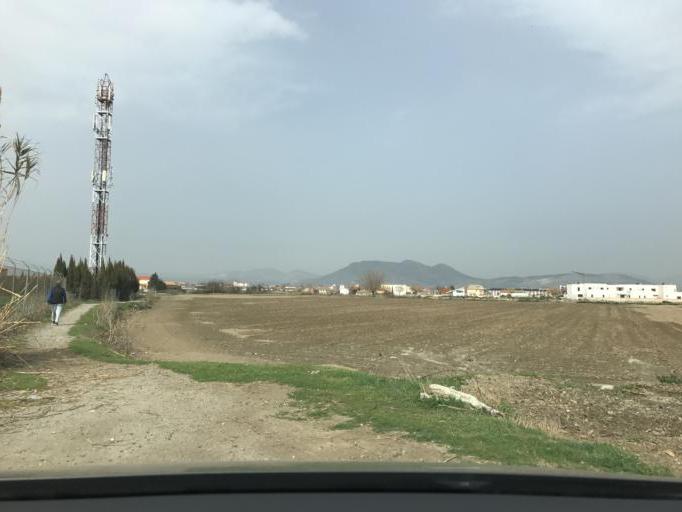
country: ES
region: Andalusia
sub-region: Provincia de Granada
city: Cullar-Vega
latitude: 37.1659
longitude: -3.6867
